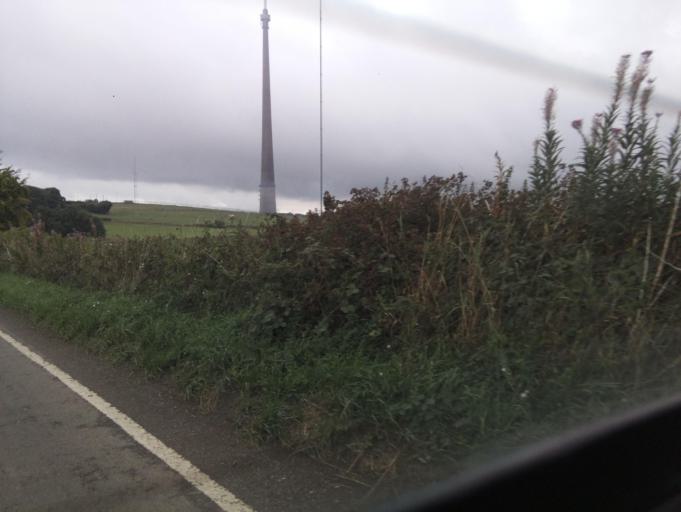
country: GB
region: England
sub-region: Kirklees
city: Shelley
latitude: 53.6091
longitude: -1.6743
